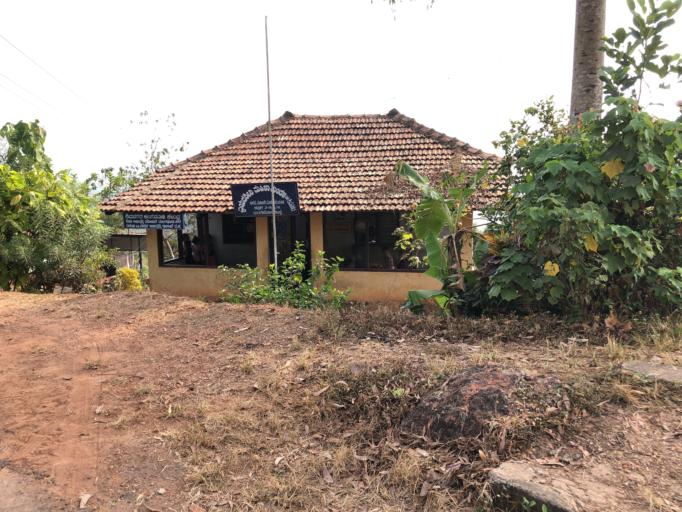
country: IN
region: Karnataka
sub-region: Dakshina Kannada
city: Mangalore
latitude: 12.8730
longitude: 74.8946
